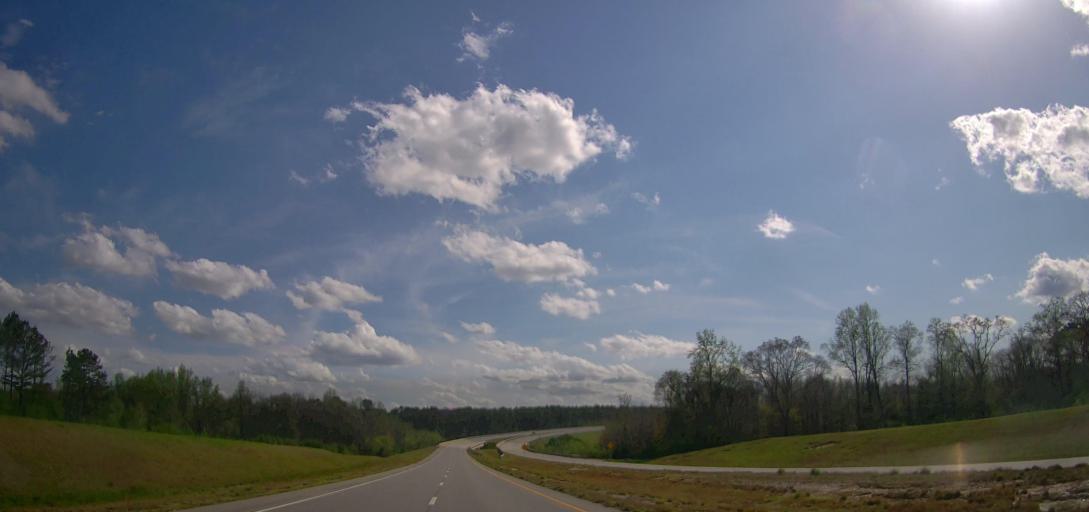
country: US
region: Georgia
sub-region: Baldwin County
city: Hardwick
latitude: 32.9867
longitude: -83.2057
